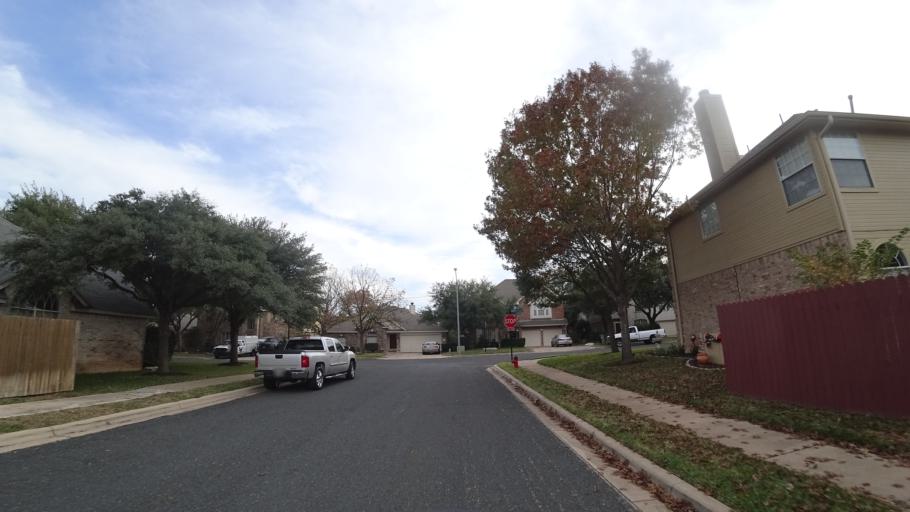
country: US
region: Texas
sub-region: Williamson County
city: Brushy Creek
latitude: 30.5128
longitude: -97.7247
